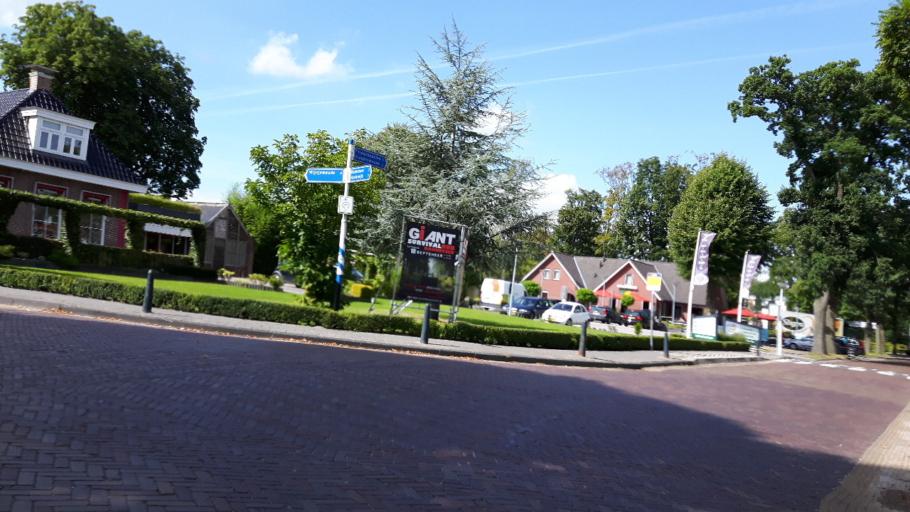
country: NL
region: Friesland
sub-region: Gemeente Smallingerland
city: Drachtstercompagnie
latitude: 53.0806
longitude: 6.2564
